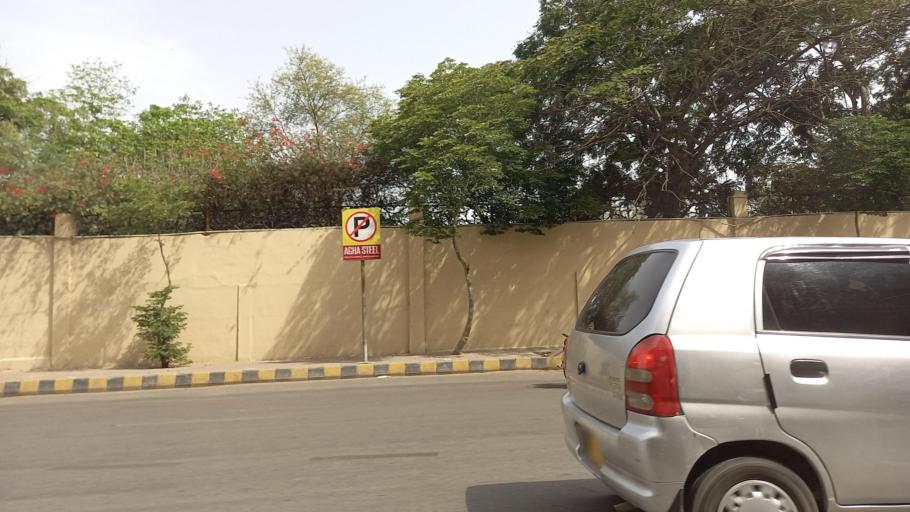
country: PK
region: Sindh
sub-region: Karachi District
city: Karachi
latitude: 24.8501
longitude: 67.0310
